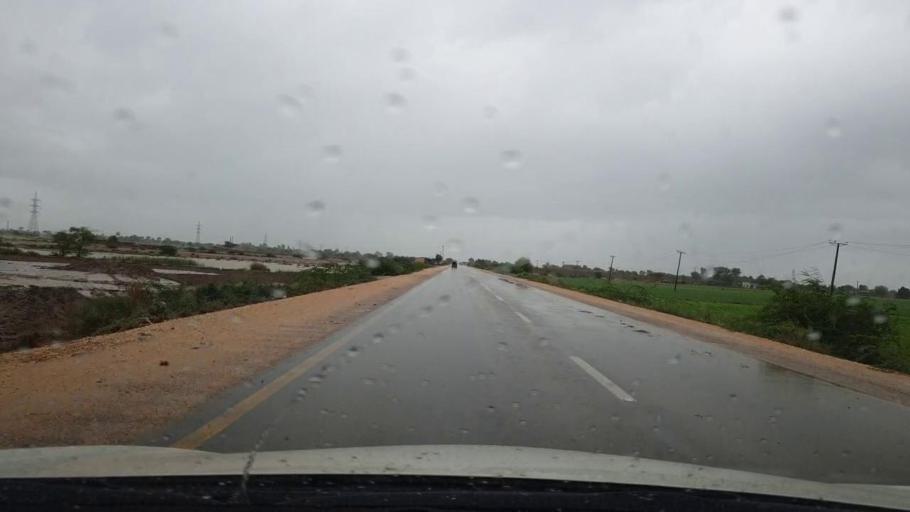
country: PK
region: Sindh
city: Kario
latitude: 24.6535
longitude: 68.5669
